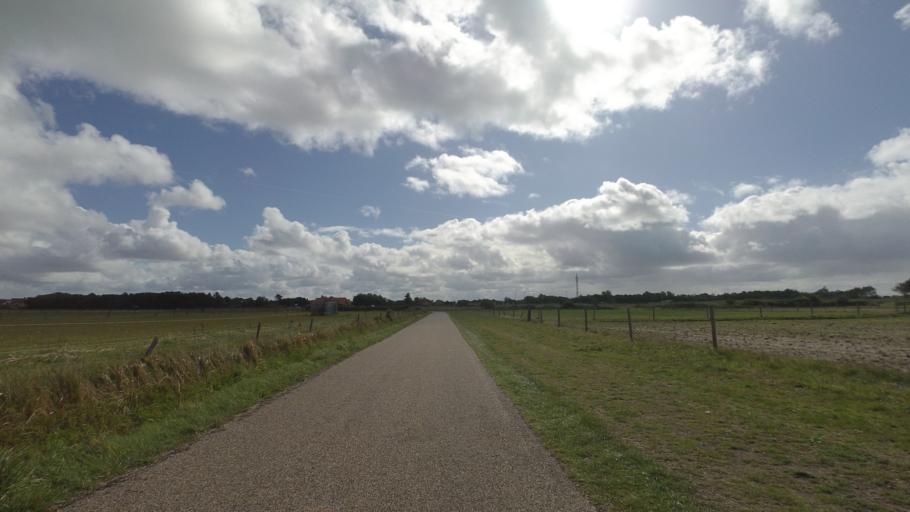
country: NL
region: Friesland
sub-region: Gemeente Ameland
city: Nes
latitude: 53.4519
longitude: 5.7924
